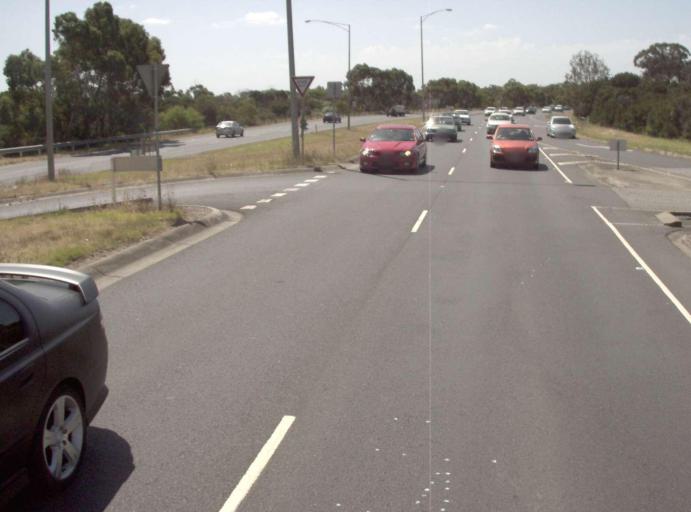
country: AU
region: Victoria
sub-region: Kingston
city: Dingley Village
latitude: -37.9691
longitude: 145.1361
